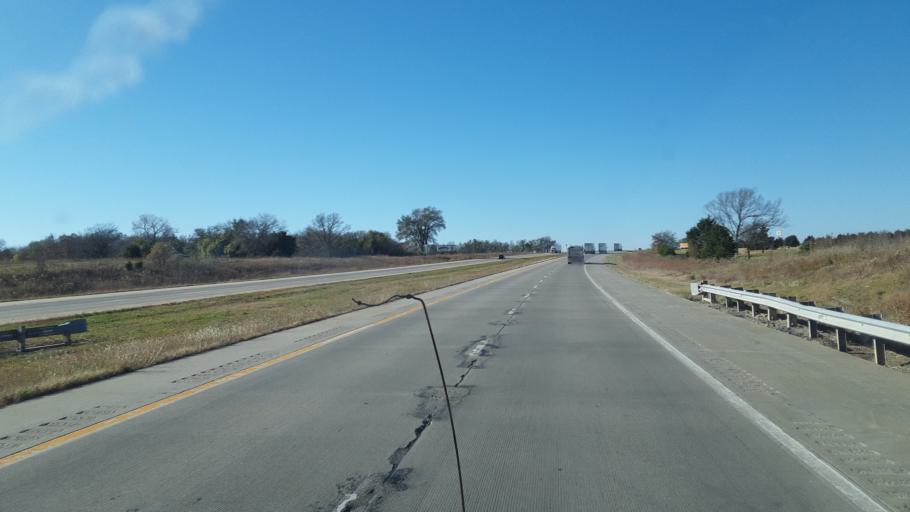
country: US
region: Kansas
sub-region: Franklin County
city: Wellsville
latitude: 38.7095
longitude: -95.0596
